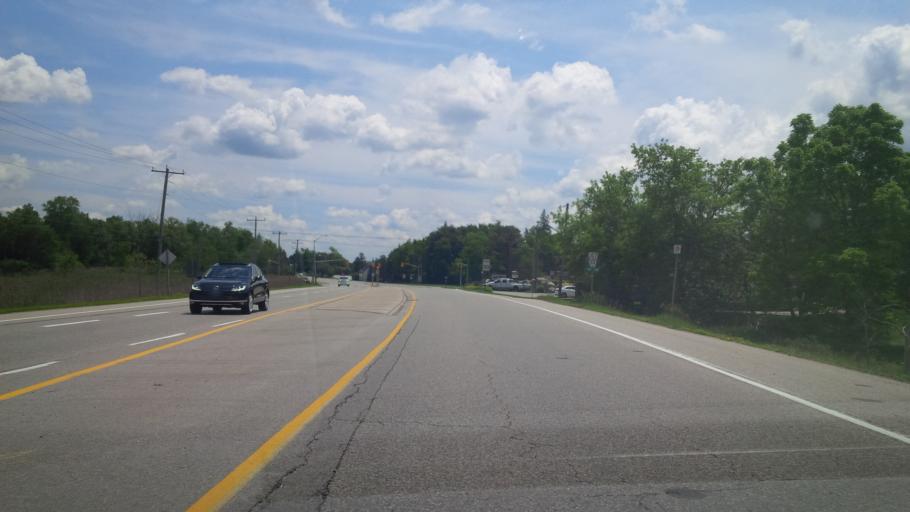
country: CA
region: Ontario
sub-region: Wellington County
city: Guelph
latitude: 43.4750
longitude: -80.1557
